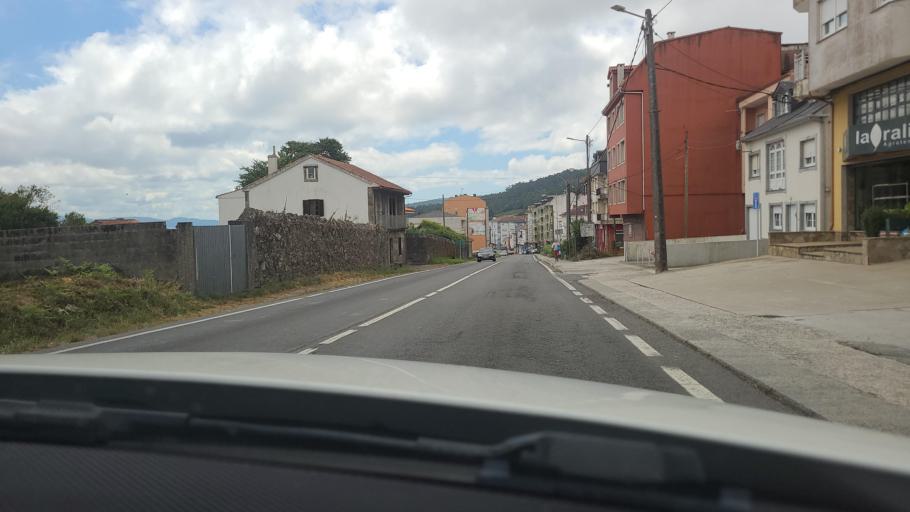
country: ES
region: Galicia
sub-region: Provincia da Coruna
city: Cee
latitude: 42.9634
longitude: -9.1935
